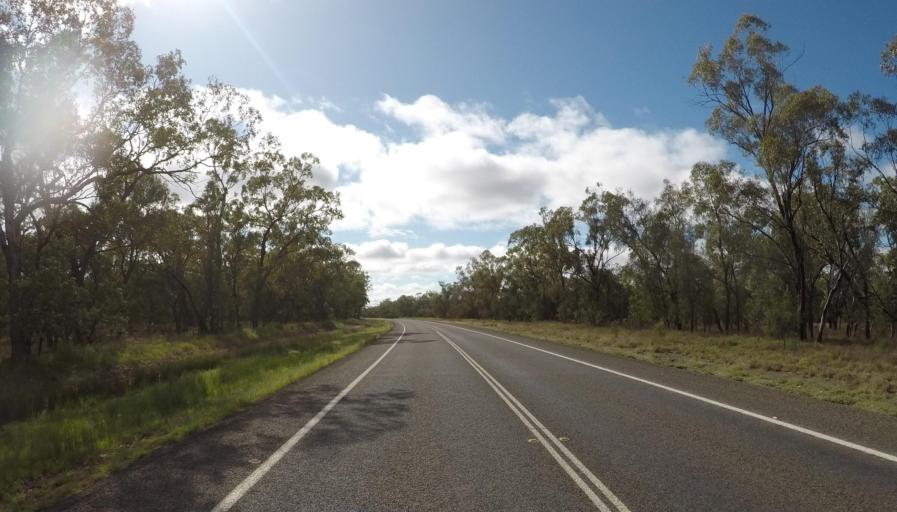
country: AU
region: Queensland
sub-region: Maranoa
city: Roma
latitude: -26.5834
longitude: 148.9688
